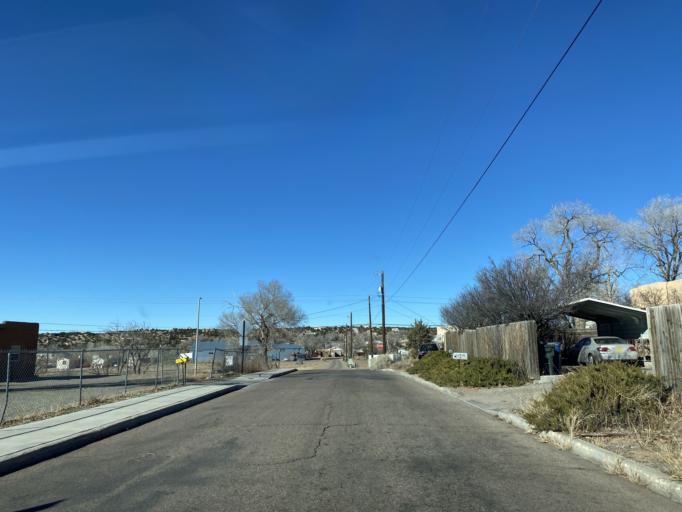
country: US
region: New Mexico
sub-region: Santa Fe County
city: Agua Fria
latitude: 35.6661
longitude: -105.9900
